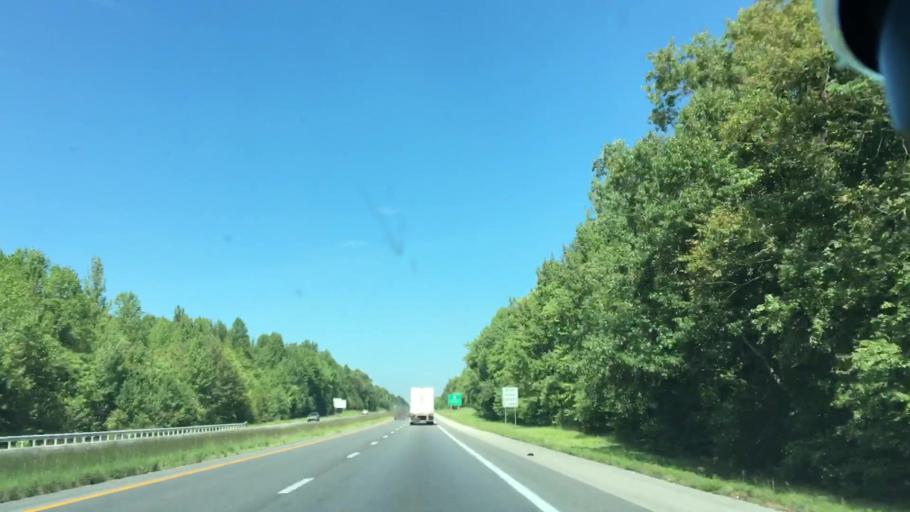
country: US
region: Kentucky
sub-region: Hopkins County
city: Earlington
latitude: 37.2608
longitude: -87.4520
